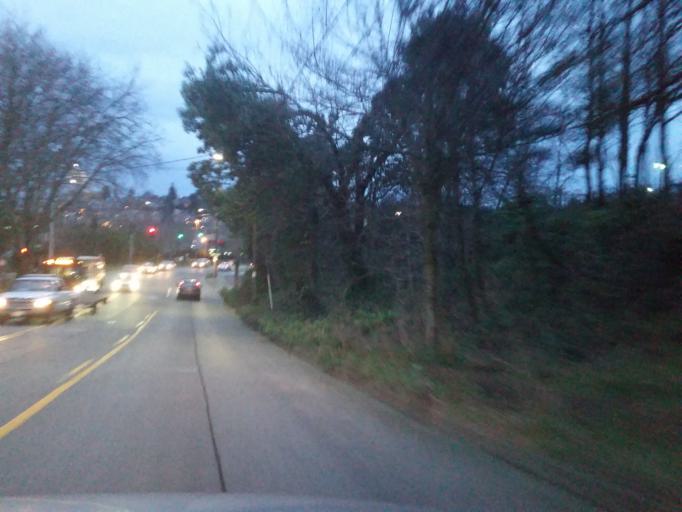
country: US
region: Washington
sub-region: King County
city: Seattle
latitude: 47.6560
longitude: -122.3845
